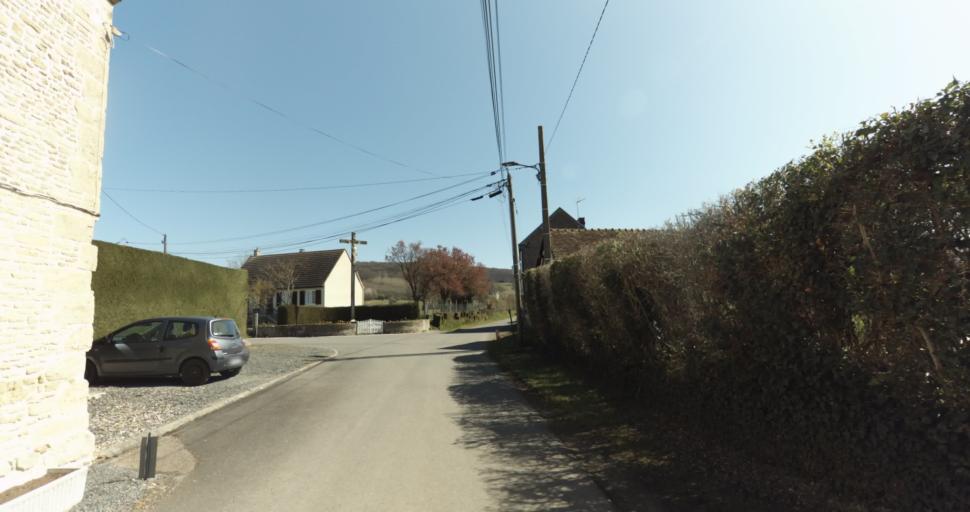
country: FR
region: Lower Normandy
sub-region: Departement du Calvados
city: Saint-Pierre-sur-Dives
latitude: 49.0091
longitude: 0.0256
